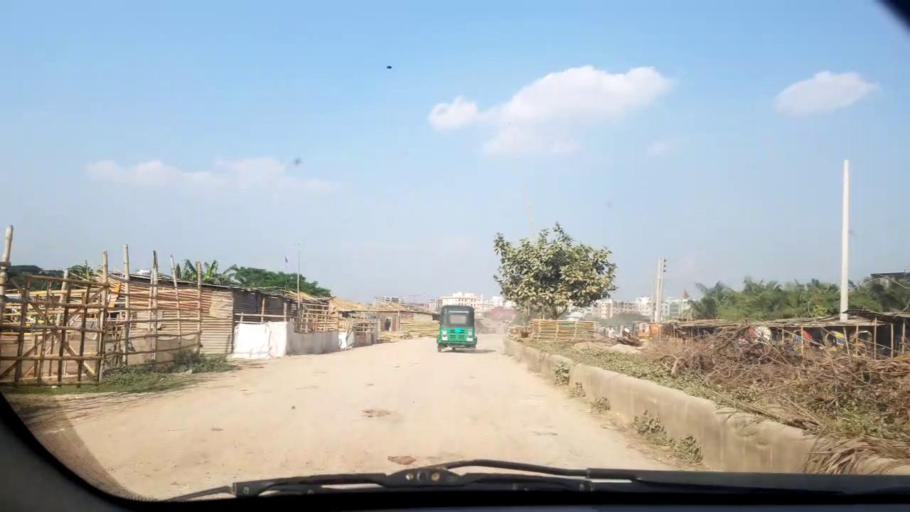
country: BD
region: Dhaka
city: Tungi
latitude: 23.8684
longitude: 90.3763
